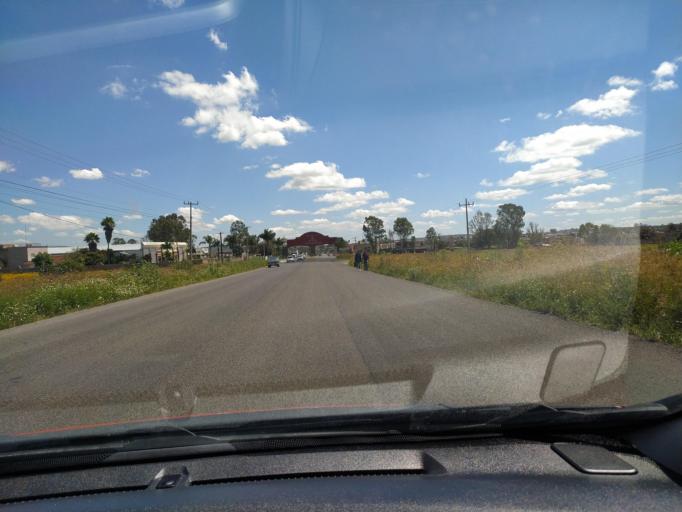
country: MX
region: Jalisco
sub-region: San Julian
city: Colonia Veintitres de Mayo
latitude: 21.0123
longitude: -102.2002
